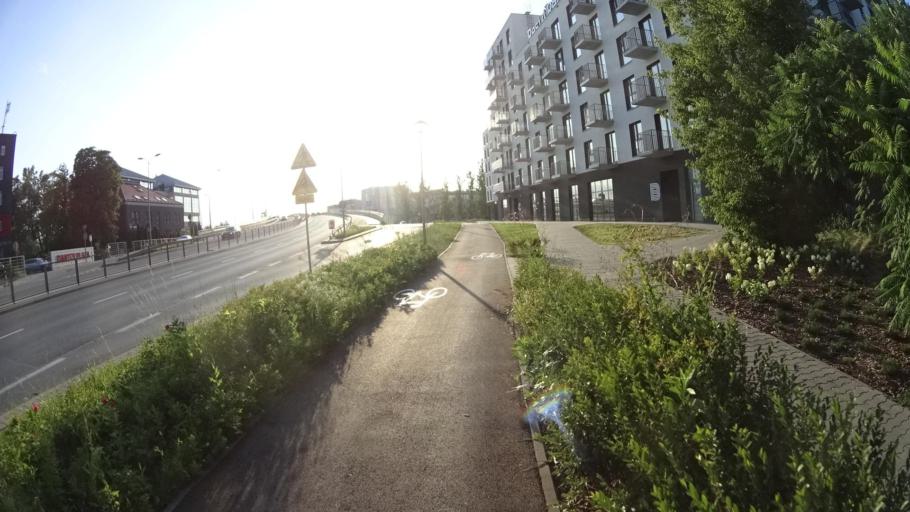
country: PL
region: Masovian Voivodeship
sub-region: Warszawa
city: Ochota
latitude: 52.1775
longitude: 20.9906
